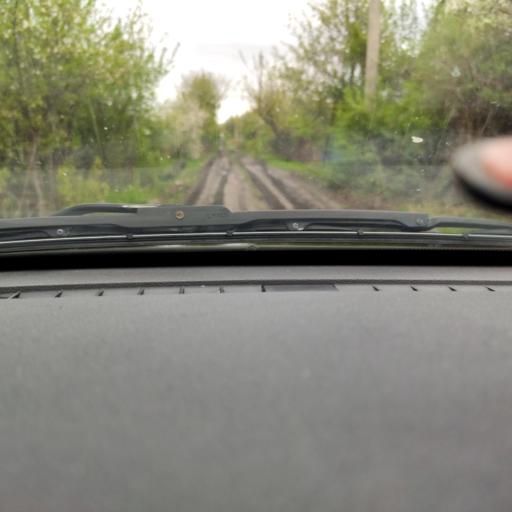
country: RU
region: Voronezj
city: Maslovka
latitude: 51.4903
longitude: 39.2186
